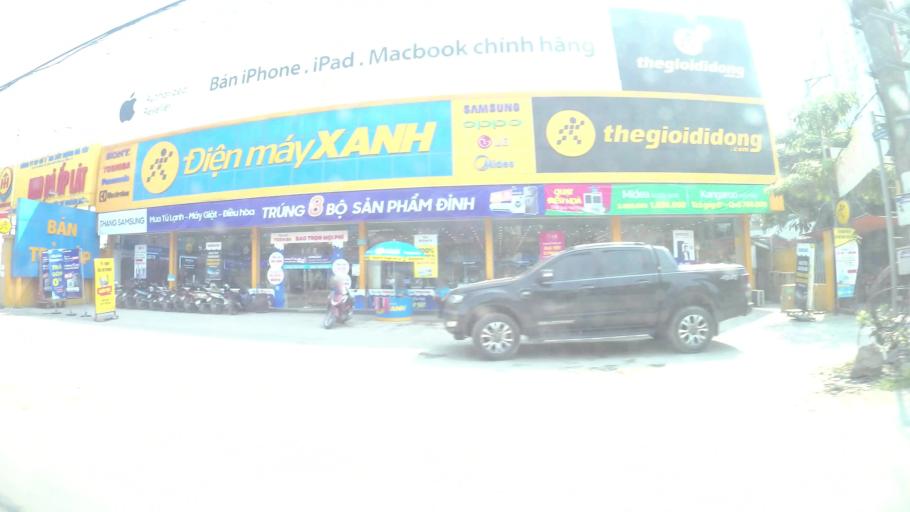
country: VN
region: Ha Noi
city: Ha Dong
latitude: 20.9601
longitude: 105.8021
